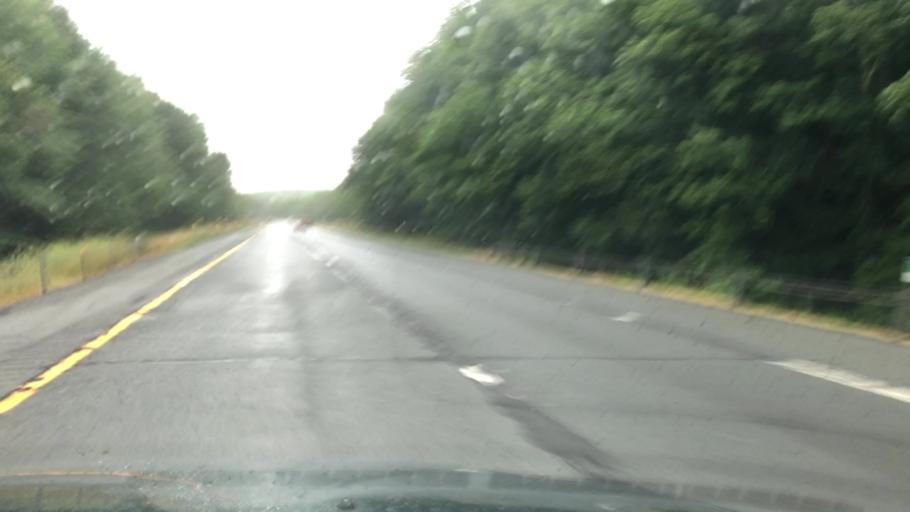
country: US
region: New York
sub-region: Orange County
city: Otisville
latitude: 41.3919
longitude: -74.5610
